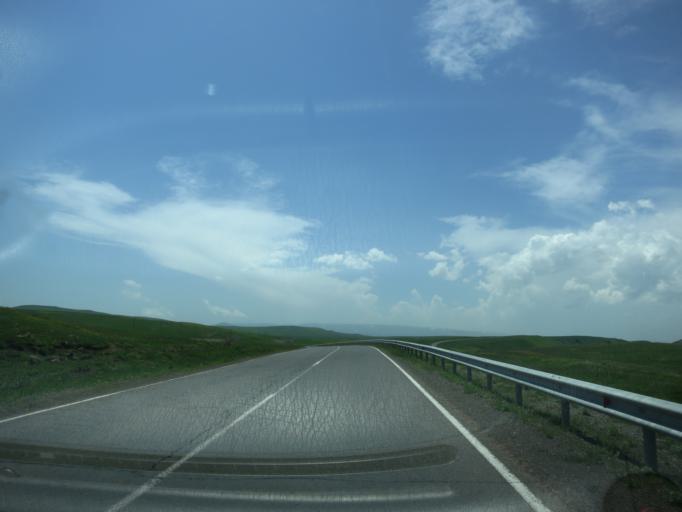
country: GE
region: Samtskhe-Javakheti
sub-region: Ninotsminda
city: Ninotsminda
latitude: 41.2947
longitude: 43.7373
